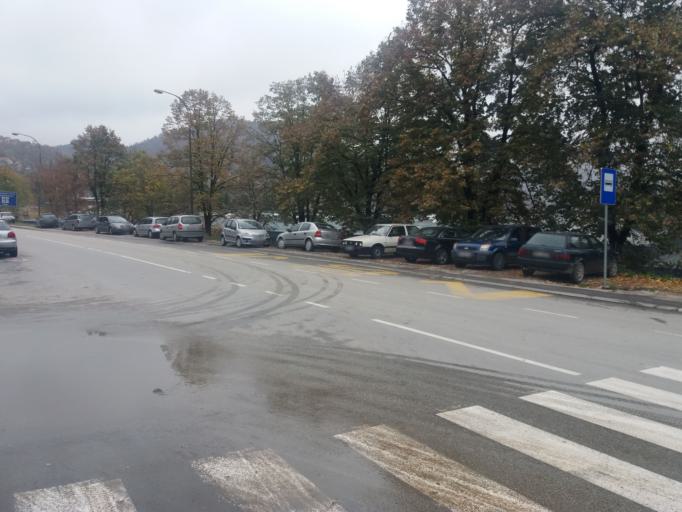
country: RS
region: Central Serbia
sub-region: Zlatiborski Okrug
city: Uzice
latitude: 43.8504
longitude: 19.8597
